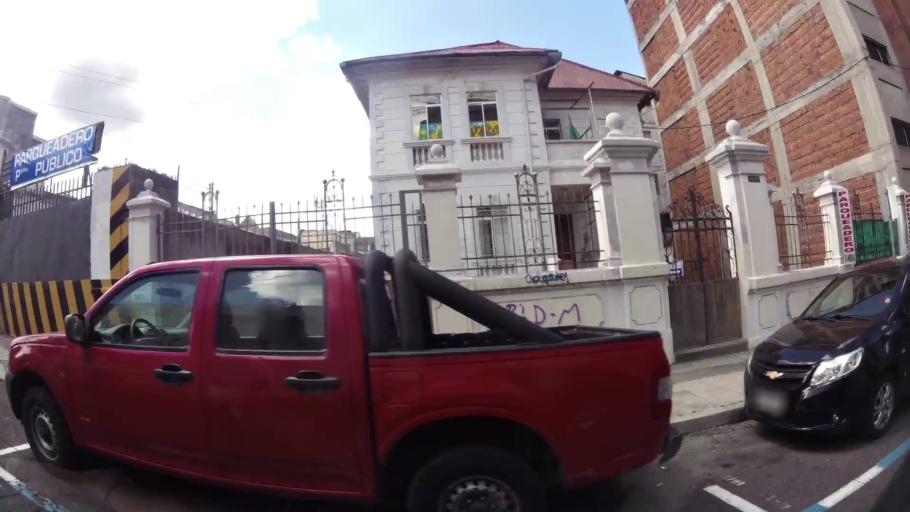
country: EC
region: Pichincha
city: Quito
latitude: -0.2073
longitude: -78.5016
